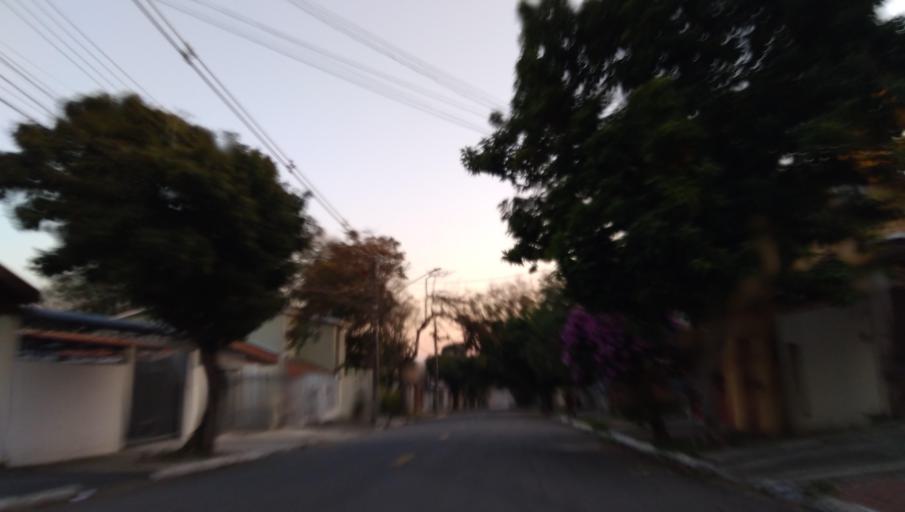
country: BR
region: Sao Paulo
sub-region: Sao Jose Dos Campos
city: Sao Jose dos Campos
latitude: -23.1794
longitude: -45.8203
